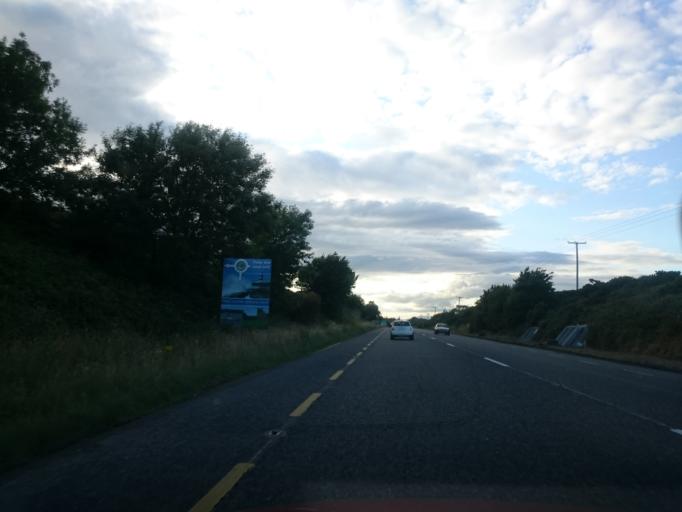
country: IE
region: Leinster
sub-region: Loch Garman
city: Loch Garman
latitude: 52.3177
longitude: -6.4955
